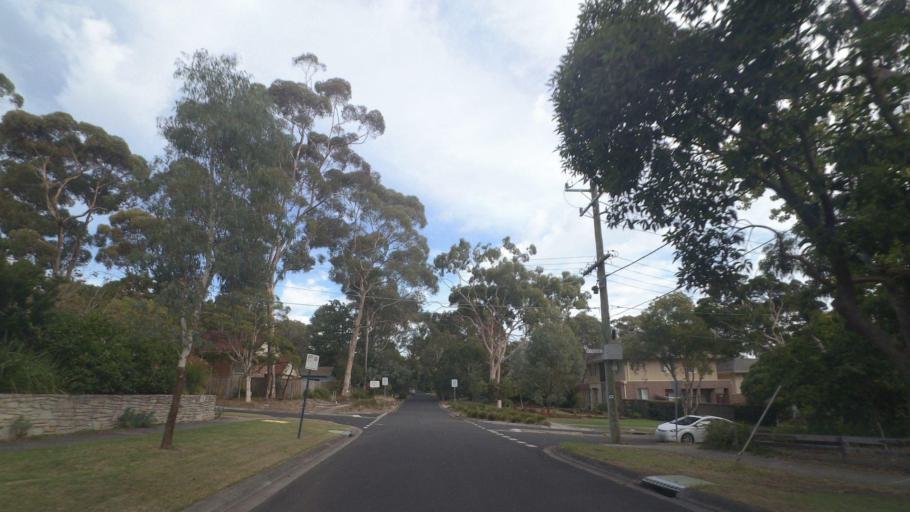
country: AU
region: Victoria
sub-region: Whitehorse
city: Blackburn
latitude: -37.8228
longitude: 145.1432
